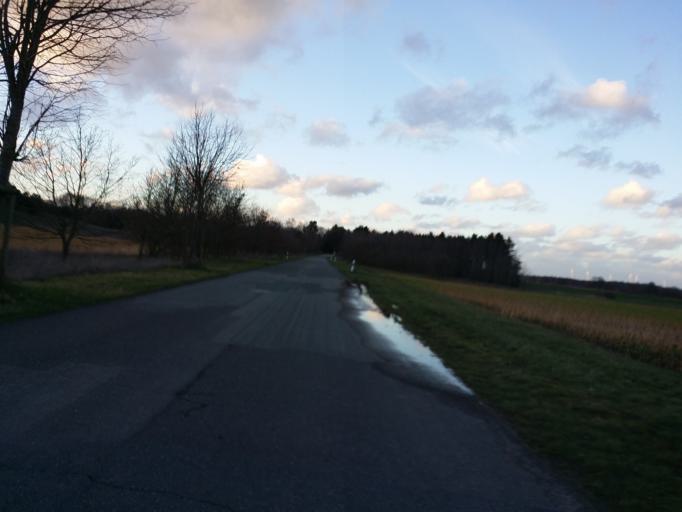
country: DE
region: Lower Saxony
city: Gross Ippener
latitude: 52.9712
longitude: 8.5976
